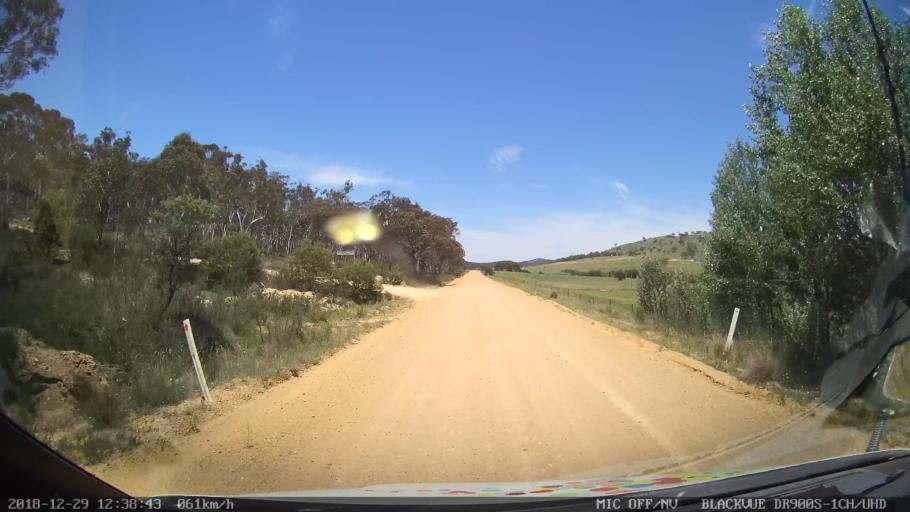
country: AU
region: Australian Capital Territory
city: Macarthur
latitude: -35.5912
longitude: 149.2286
